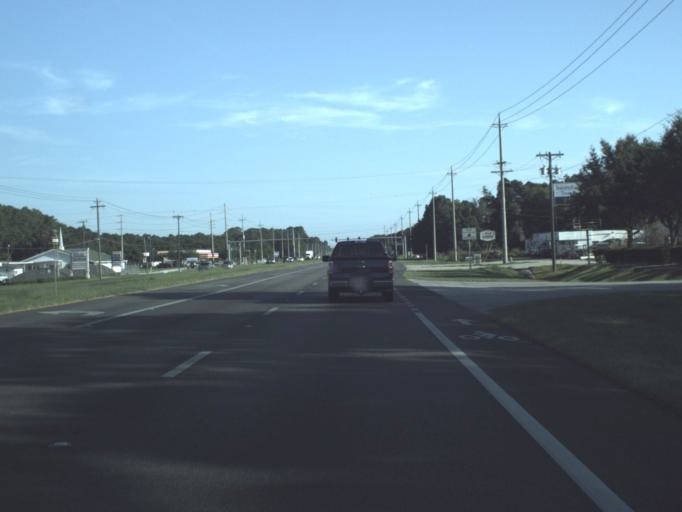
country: US
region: Florida
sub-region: Polk County
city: Gibsonia
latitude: 28.1475
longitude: -81.9736
